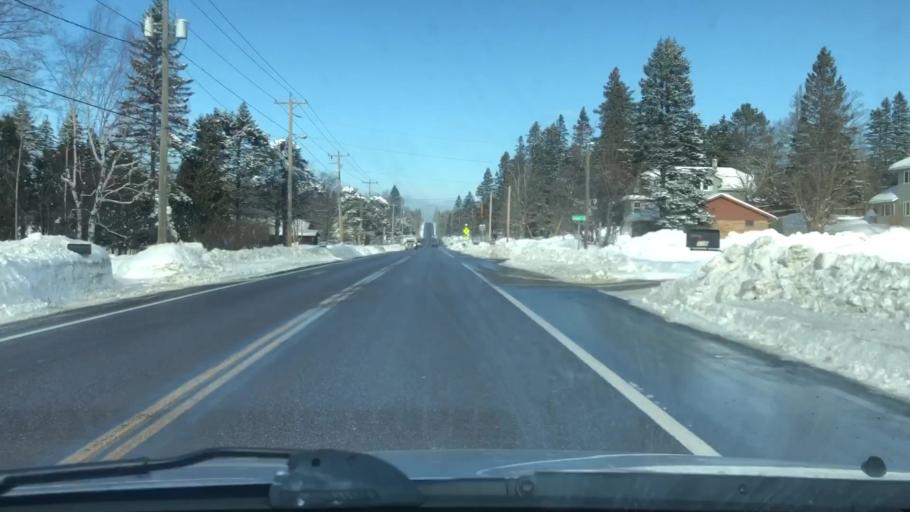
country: US
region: Minnesota
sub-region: Saint Louis County
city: Duluth
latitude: 46.8026
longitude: -92.1322
